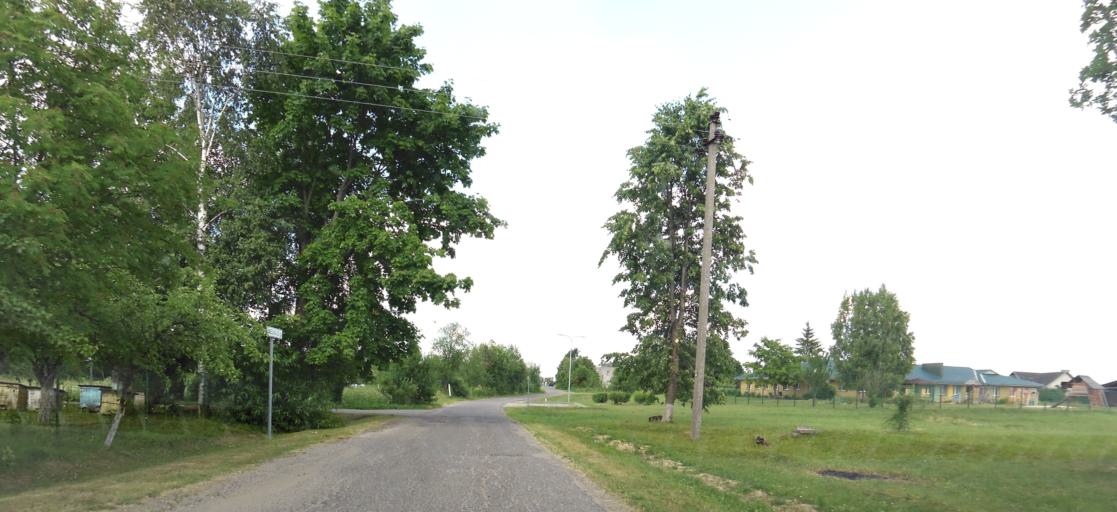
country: LT
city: Skaidiskes
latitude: 54.5344
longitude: 25.6497
